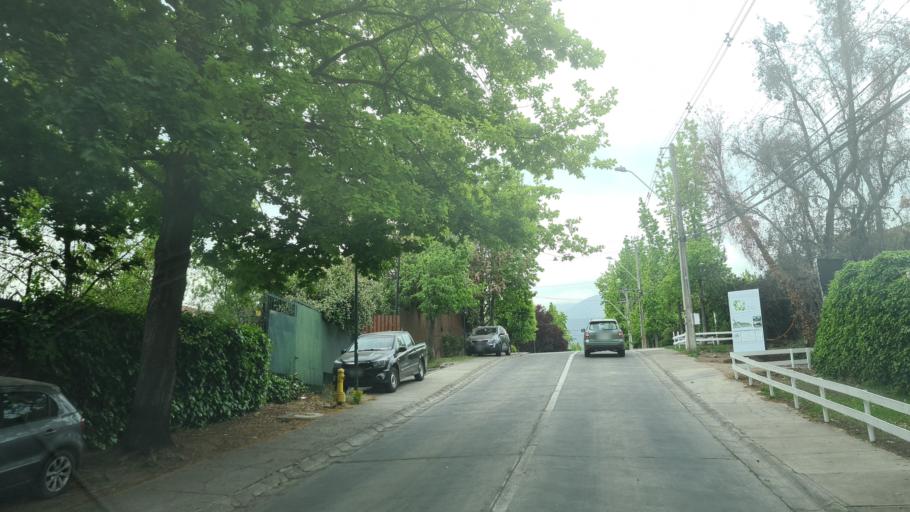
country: CL
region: Santiago Metropolitan
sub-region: Provincia de Santiago
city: Villa Presidente Frei, Nunoa, Santiago, Chile
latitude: -33.3418
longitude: -70.5073
